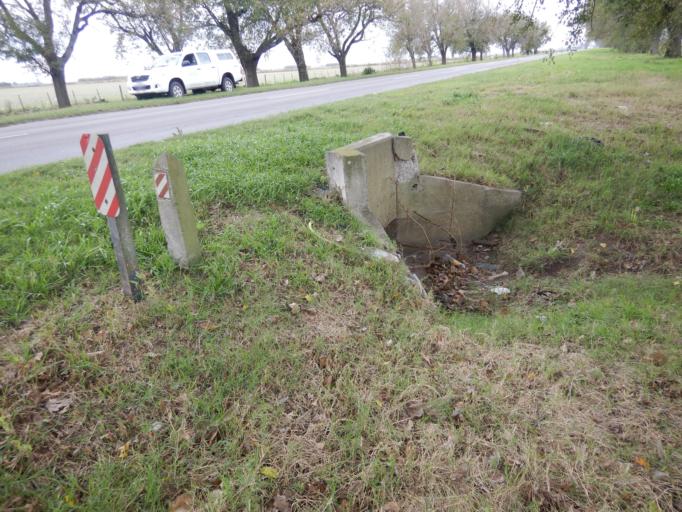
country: AR
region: Santa Fe
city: Carcarana
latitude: -32.8708
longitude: -61.1043
